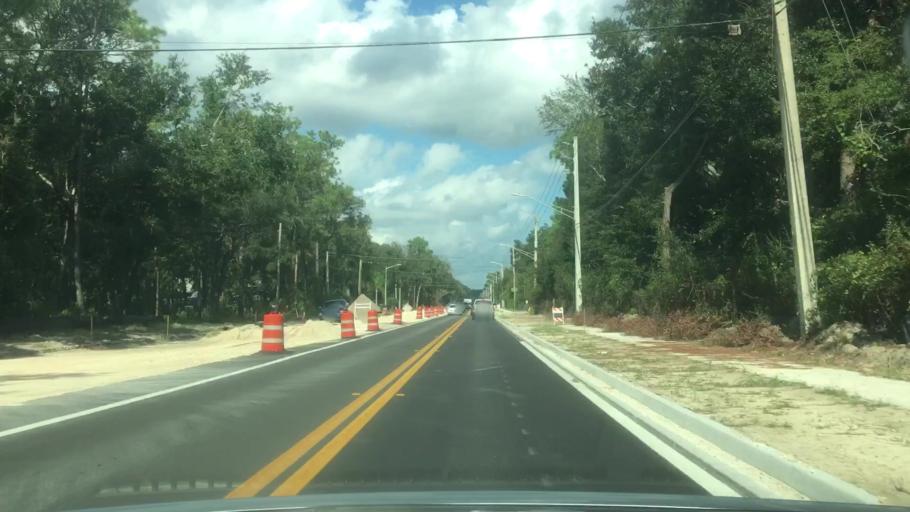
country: US
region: Florida
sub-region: Duval County
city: Atlantic Beach
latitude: 30.3409
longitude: -81.4617
